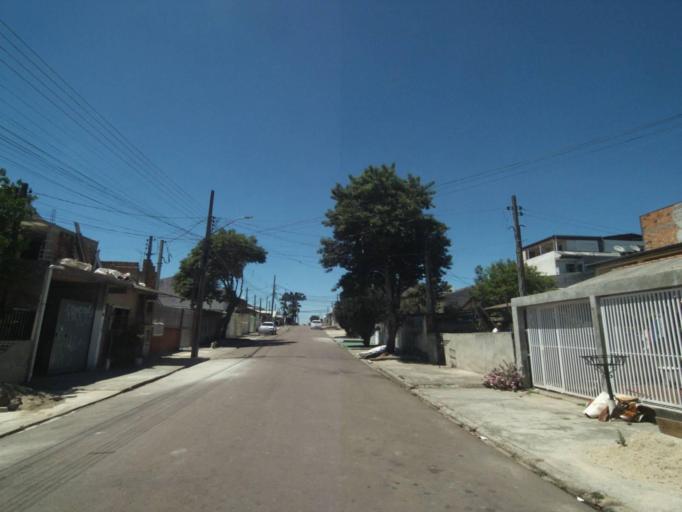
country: BR
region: Parana
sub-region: Curitiba
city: Curitiba
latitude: -25.4730
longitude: -49.3515
